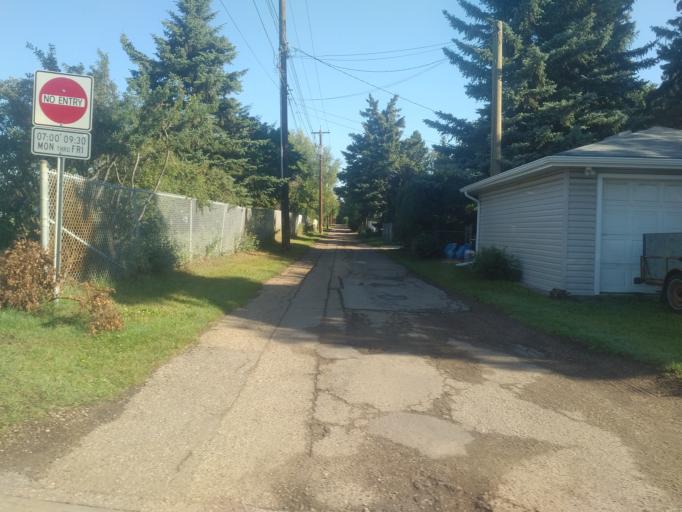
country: CA
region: Alberta
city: Edmonton
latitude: 53.5040
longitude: -113.5225
